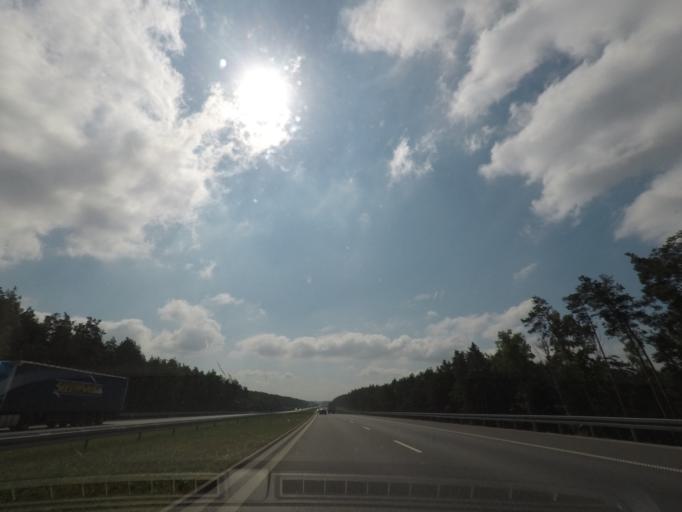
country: PL
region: Kujawsko-Pomorskie
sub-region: Powiat aleksandrowski
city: Aleksandrow Kujawski
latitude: 52.8901
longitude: 18.7303
